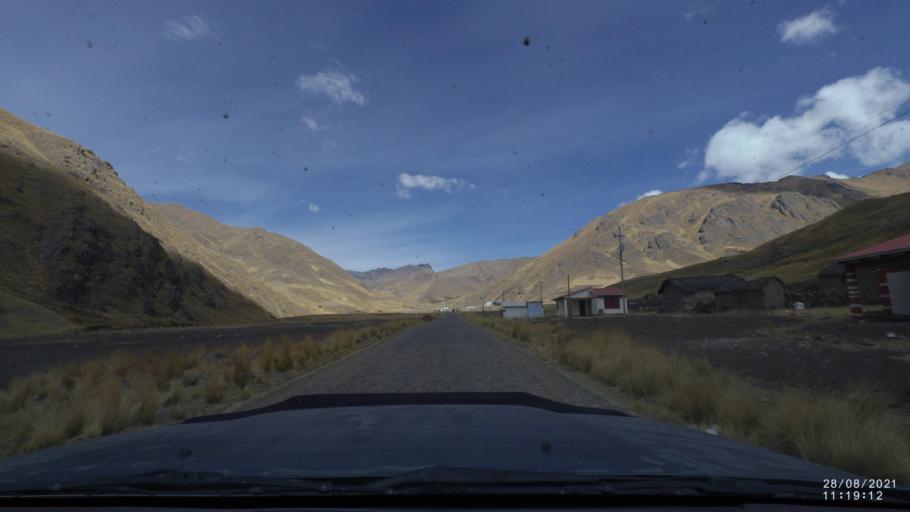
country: BO
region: Cochabamba
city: Cochabamba
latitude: -17.1522
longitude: -66.3301
